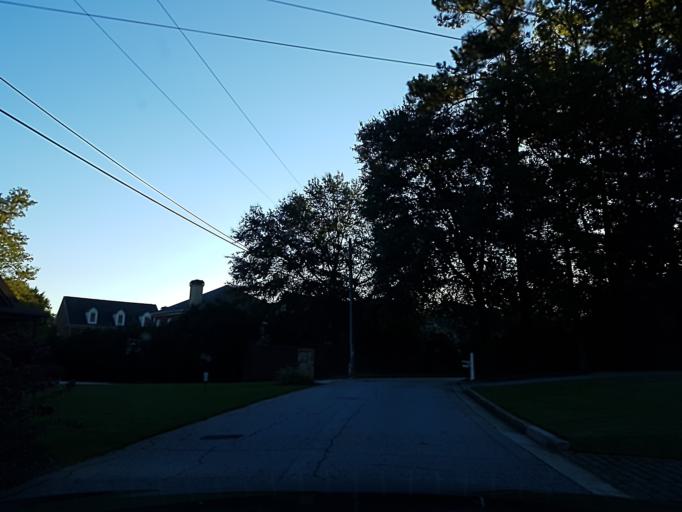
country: US
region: Georgia
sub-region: Cobb County
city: Vinings
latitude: 33.8626
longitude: -84.4939
